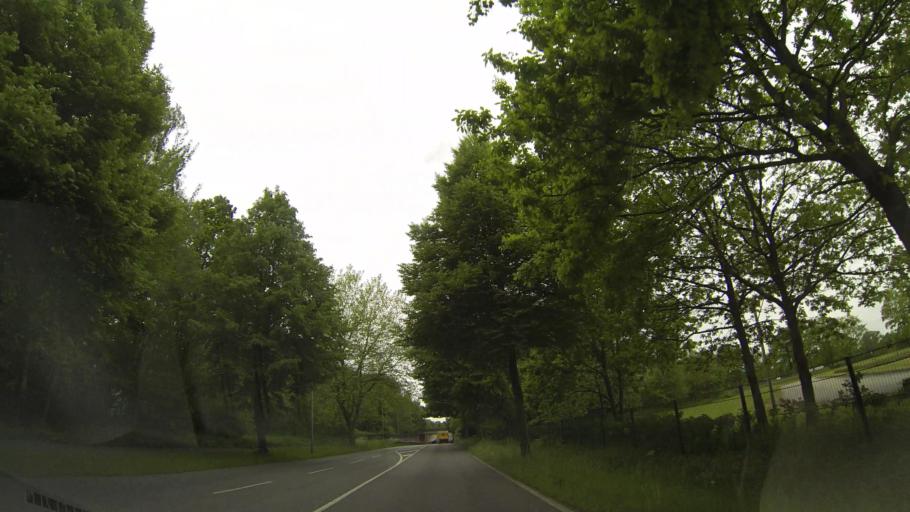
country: DE
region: Schleswig-Holstein
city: Halstenbek
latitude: 53.6216
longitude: 9.8609
